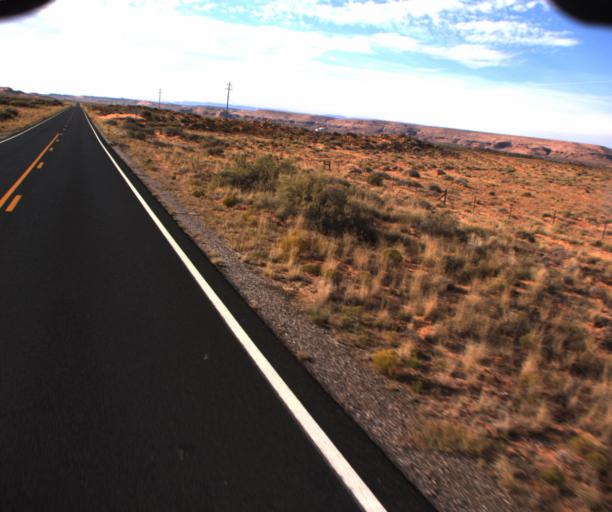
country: US
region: Arizona
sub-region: Apache County
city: Many Farms
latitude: 36.8113
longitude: -109.6470
